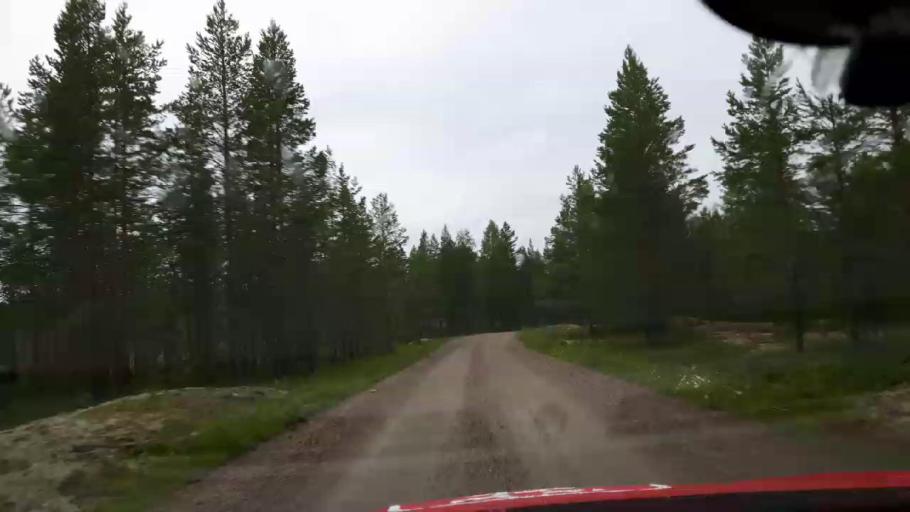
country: SE
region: Jaemtland
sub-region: OEstersunds Kommun
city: Brunflo
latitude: 62.8118
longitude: 14.8840
